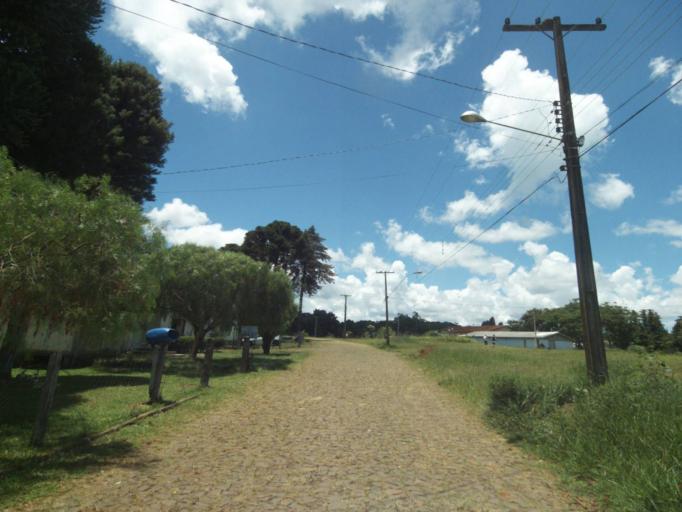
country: BR
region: Parana
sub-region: Pinhao
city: Pinhao
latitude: -25.7909
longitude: -52.0850
